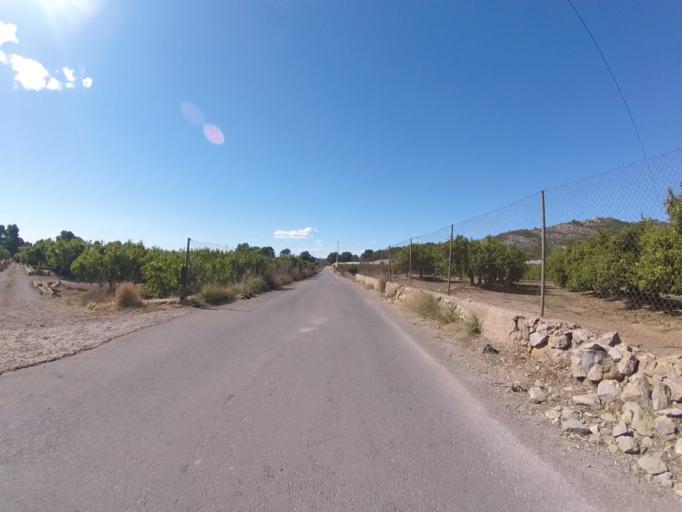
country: ES
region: Valencia
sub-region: Provincia de Castello
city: Benicassim
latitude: 40.0673
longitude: 0.0738
